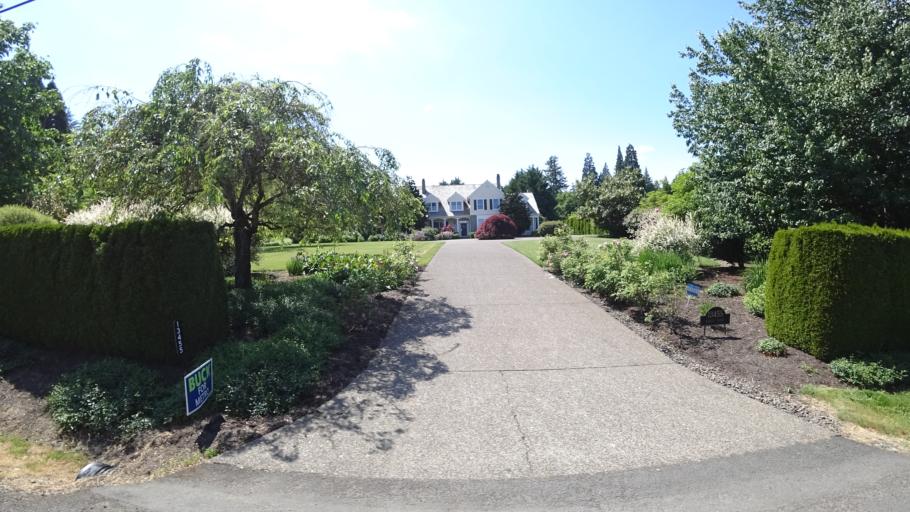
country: US
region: Oregon
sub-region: Clackamas County
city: Lake Oswego
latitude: 45.4279
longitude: -122.6923
